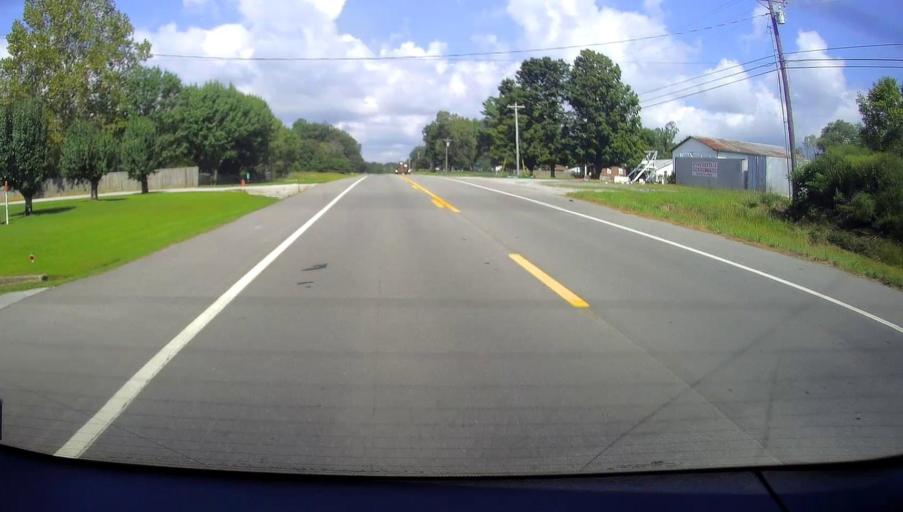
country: US
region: Tennessee
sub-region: Coffee County
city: Manchester
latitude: 35.5107
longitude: -86.1237
